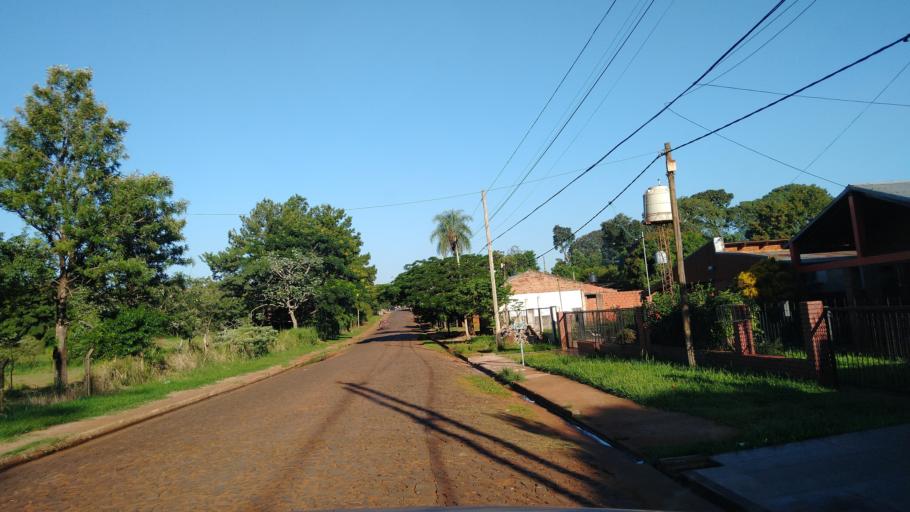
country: AR
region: Misiones
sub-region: Departamento de Capital
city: Posadas
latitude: -27.4060
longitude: -55.9268
